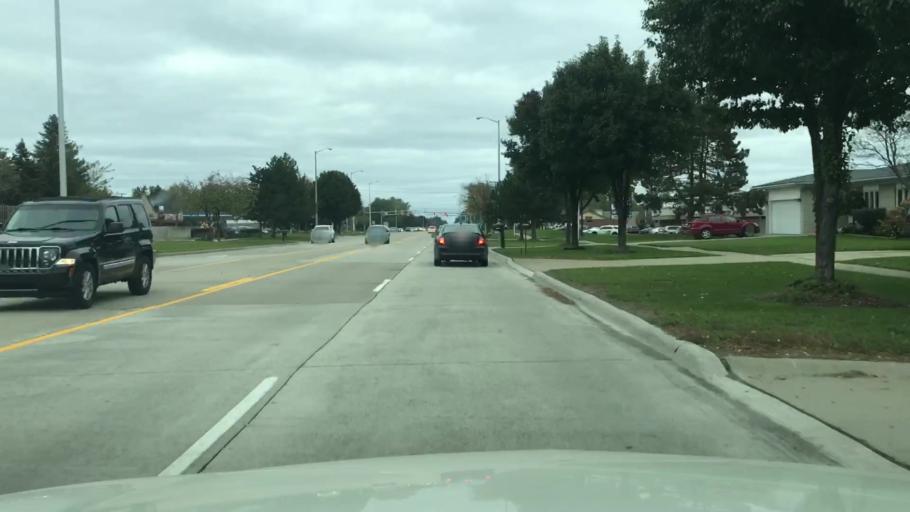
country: US
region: Michigan
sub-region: Macomb County
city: Sterling Heights
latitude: 42.5620
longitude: -83.0697
